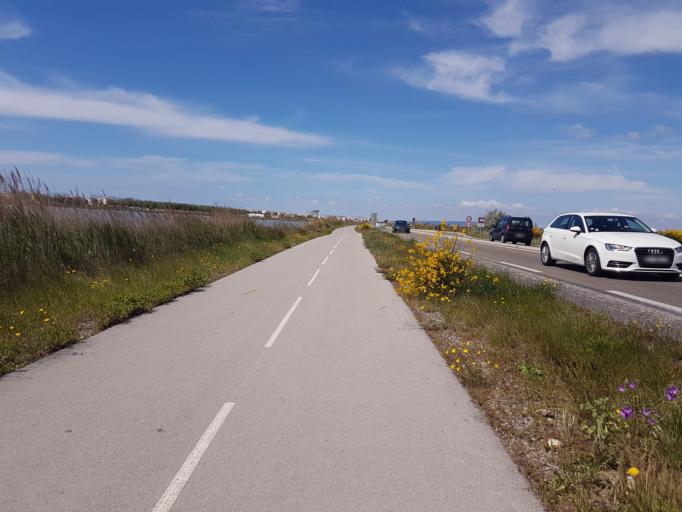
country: FR
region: Languedoc-Roussillon
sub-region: Departement de l'Herault
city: Perols
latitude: 43.5387
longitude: 3.9534
